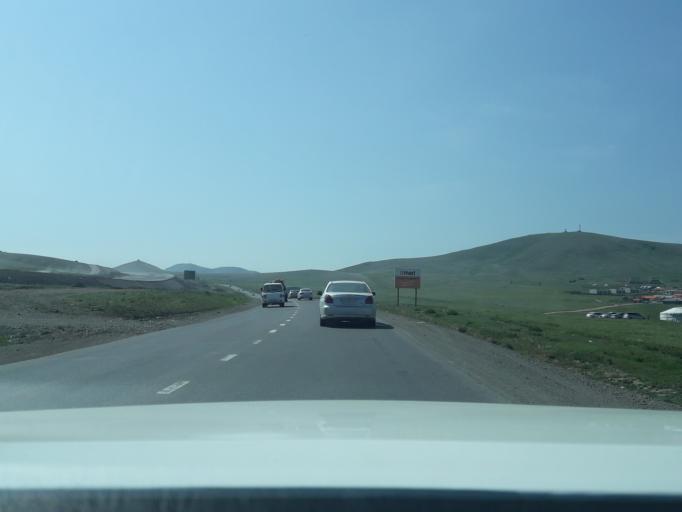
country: MN
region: Ulaanbaatar
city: Ulaanbaatar
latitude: 47.8007
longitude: 106.7466
